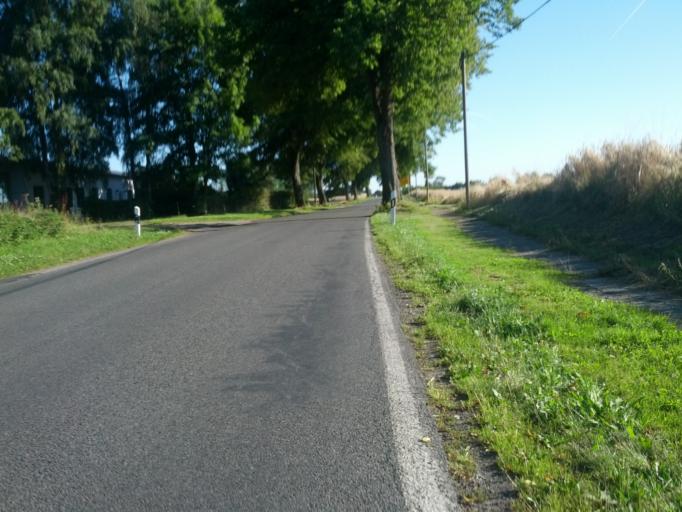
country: DE
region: Mecklenburg-Vorpommern
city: Bastorf
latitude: 54.1081
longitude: 11.6800
